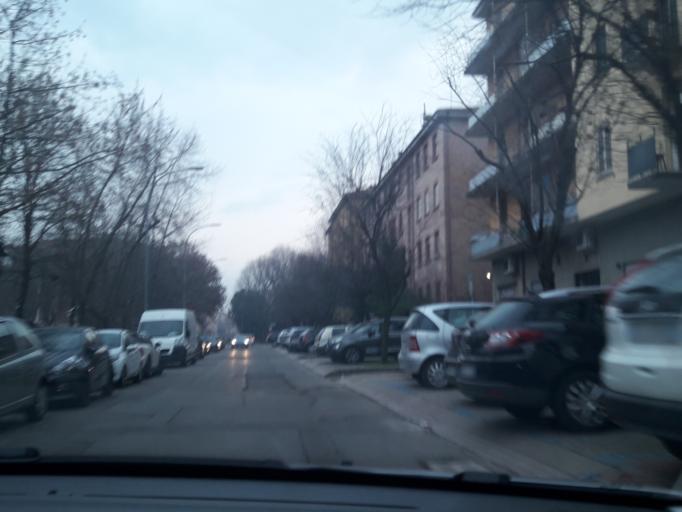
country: IT
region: Emilia-Romagna
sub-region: Provincia di Bologna
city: Bologna
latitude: 44.5030
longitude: 11.3108
